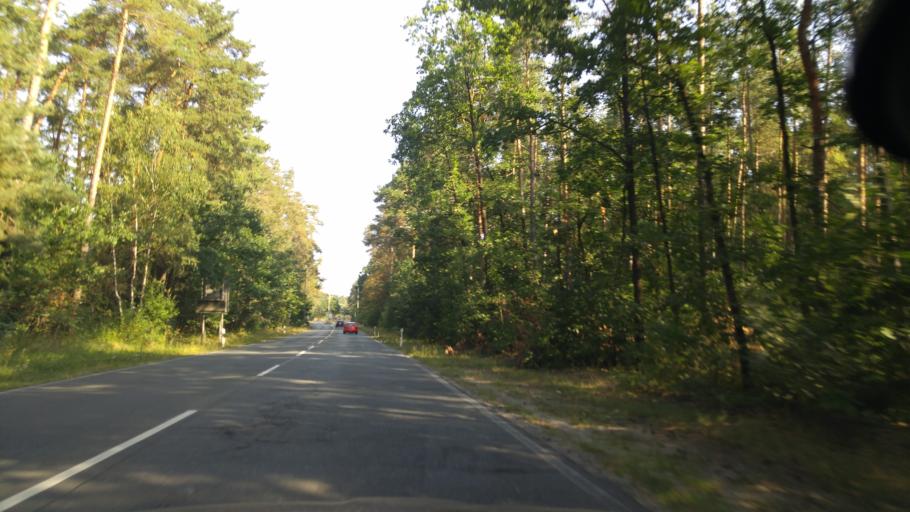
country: DE
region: Bavaria
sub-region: Regierungsbezirk Mittelfranken
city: Buckenhof
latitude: 49.5703
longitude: 11.0316
